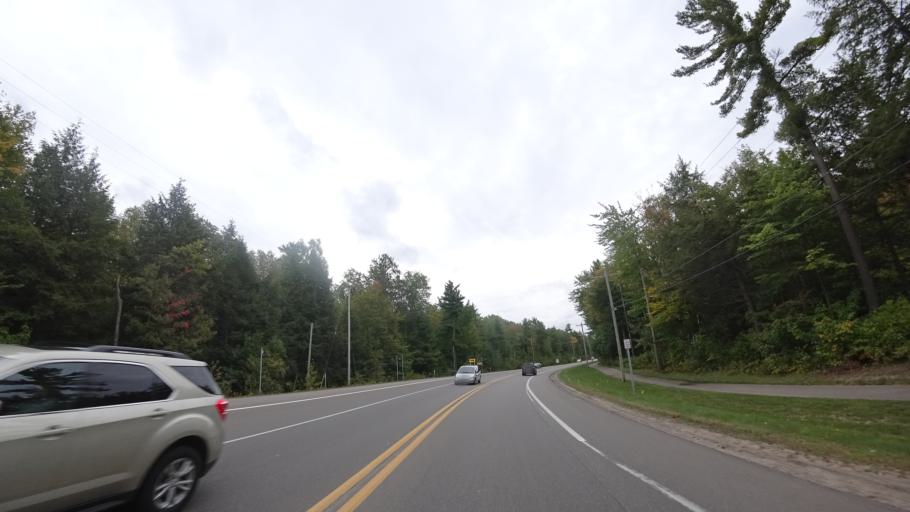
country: US
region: Michigan
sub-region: Emmet County
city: Petoskey
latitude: 45.4106
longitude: -84.9026
